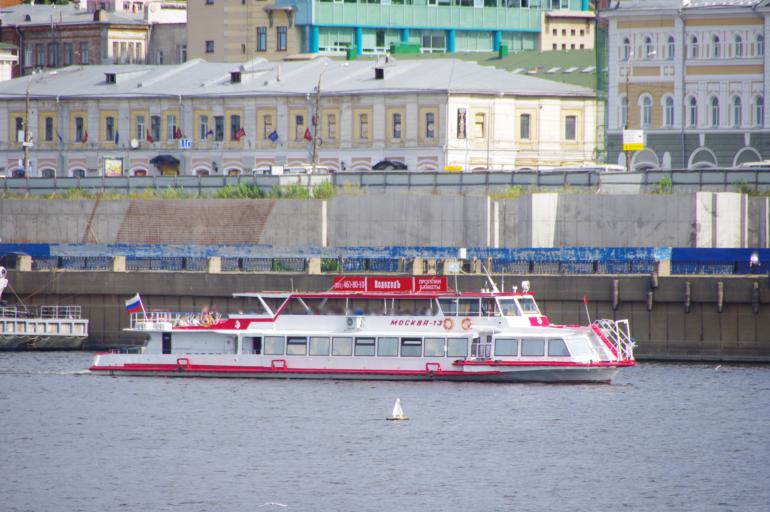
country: RU
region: Nizjnij Novgorod
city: Nizhniy Novgorod
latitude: 56.3333
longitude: 43.9855
